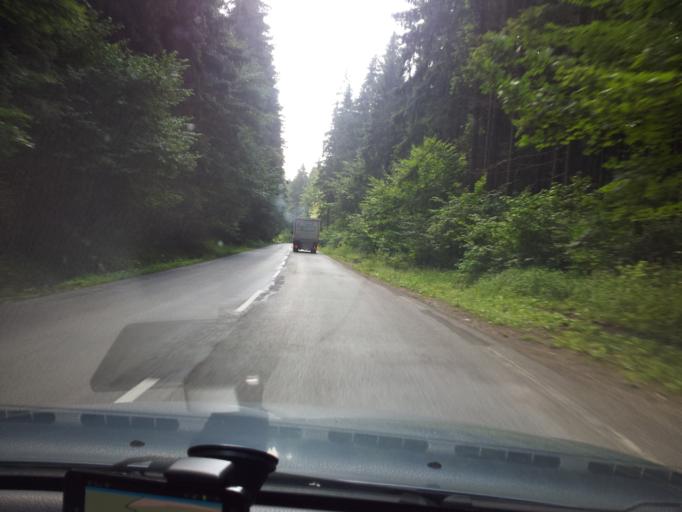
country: SK
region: Zilinsky
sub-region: Okres Dolny Kubin
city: Dolny Kubin
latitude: 49.2892
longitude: 19.3491
